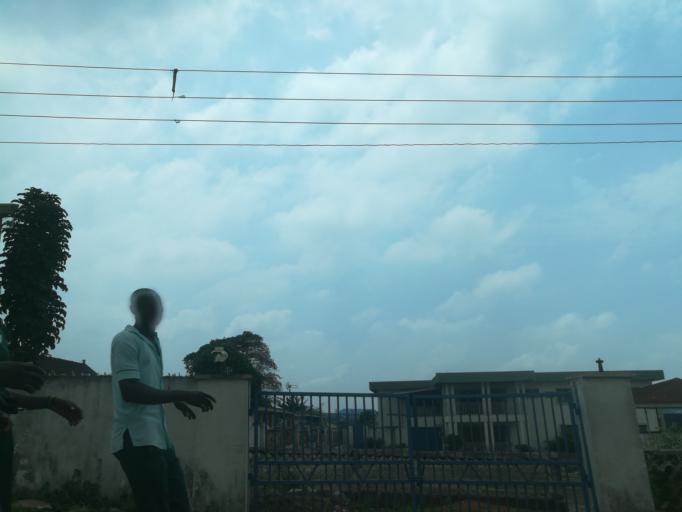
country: NG
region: Lagos
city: Ikorodu
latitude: 6.6174
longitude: 3.5152
